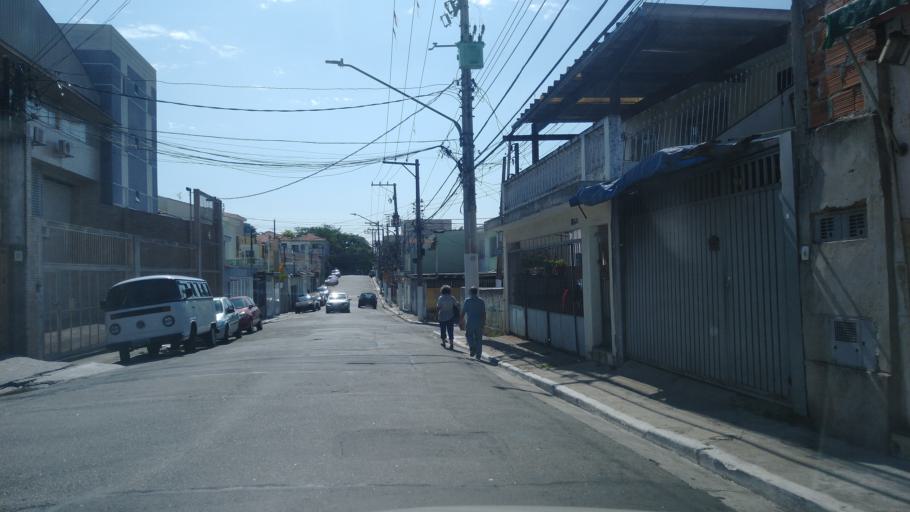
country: BR
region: Sao Paulo
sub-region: Guarulhos
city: Guarulhos
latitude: -23.4800
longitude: -46.5966
